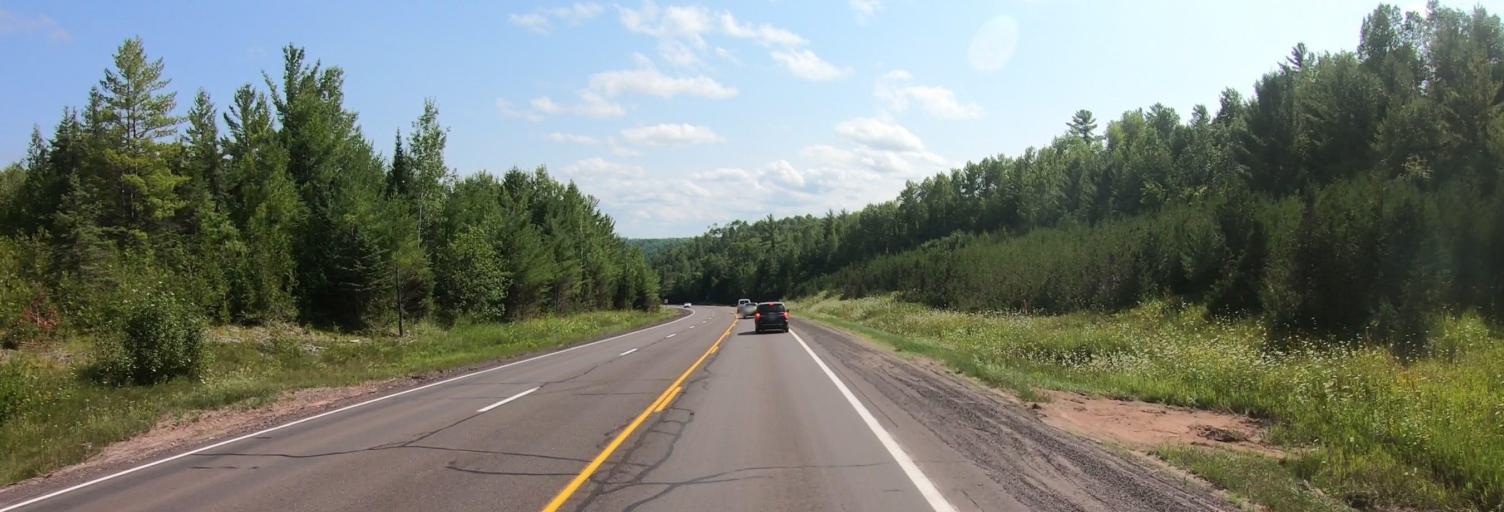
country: US
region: Michigan
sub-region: Ontonagon County
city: Ontonagon
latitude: 46.7102
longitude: -89.1598
